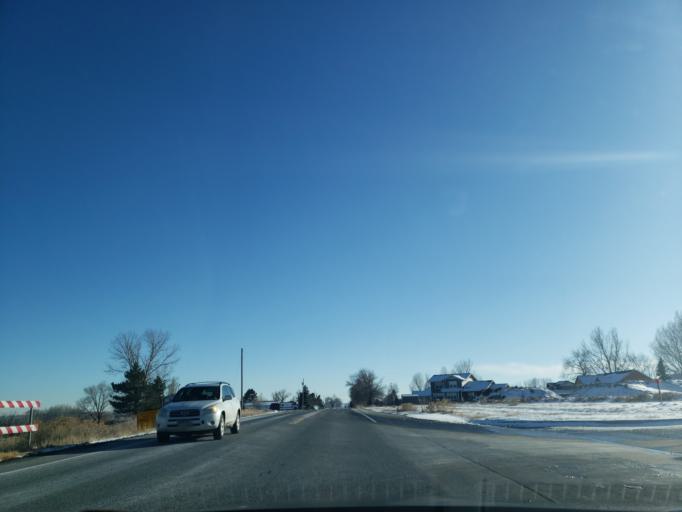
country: US
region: Colorado
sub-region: Weld County
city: Windsor
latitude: 40.5143
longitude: -105.0010
